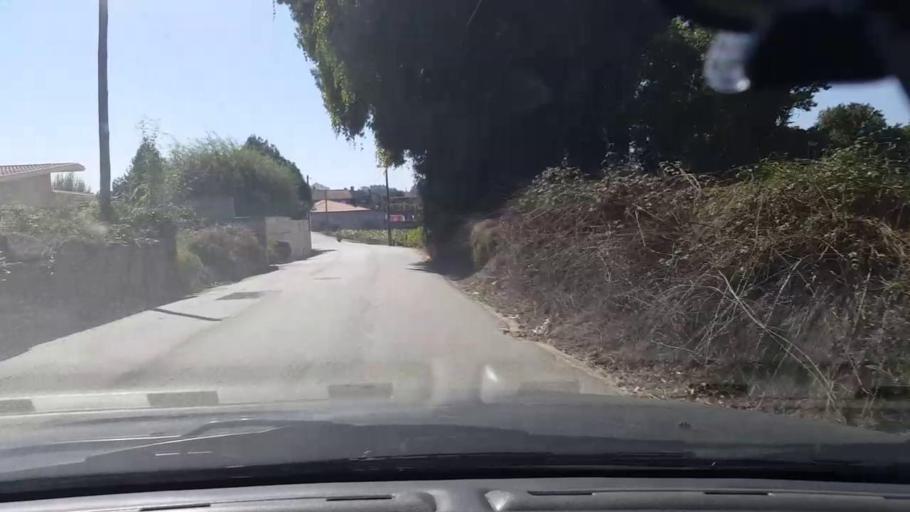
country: PT
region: Porto
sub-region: Matosinhos
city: Lavra
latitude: 41.2706
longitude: -8.6902
